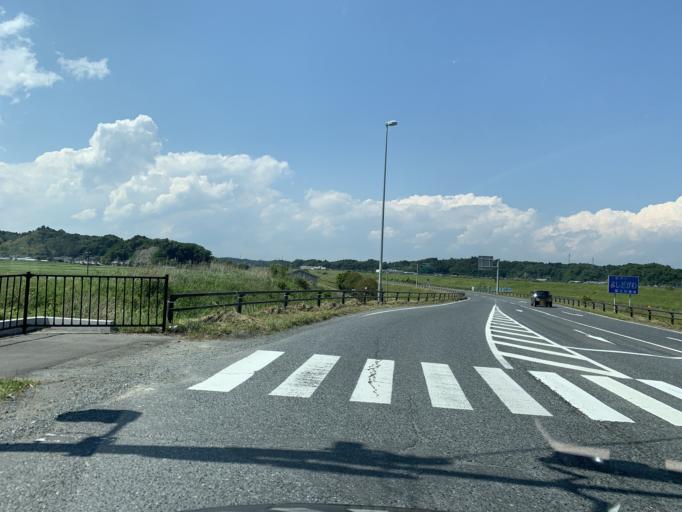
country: JP
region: Miyagi
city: Yamoto
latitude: 38.3958
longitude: 141.1553
